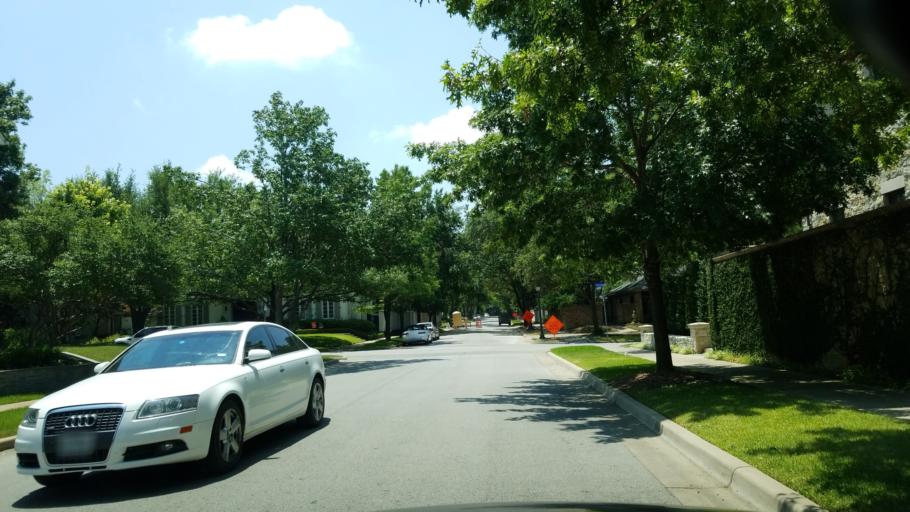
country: US
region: Texas
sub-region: Dallas County
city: Highland Park
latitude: 32.8305
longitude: -96.7891
